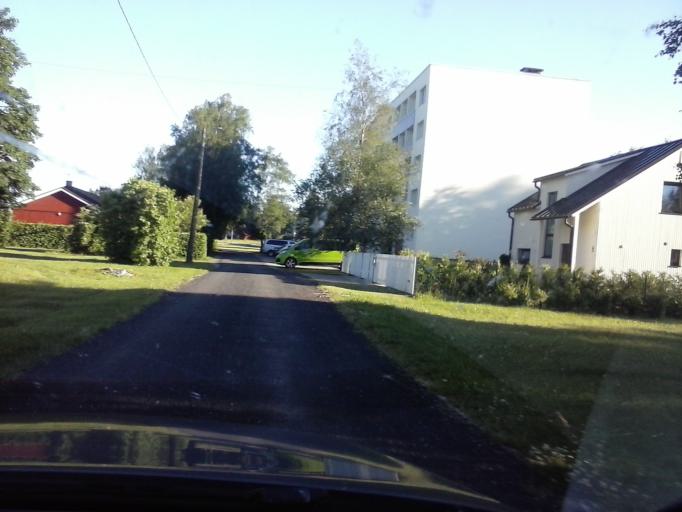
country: EE
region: Raplamaa
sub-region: Rapla vald
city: Rapla
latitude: 58.9986
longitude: 24.7853
